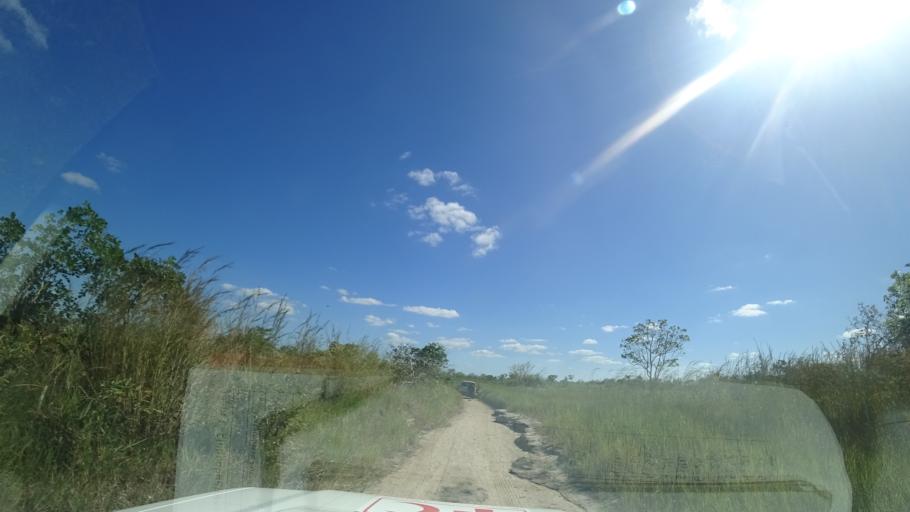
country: MZ
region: Sofala
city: Dondo
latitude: -19.4772
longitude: 34.6282
